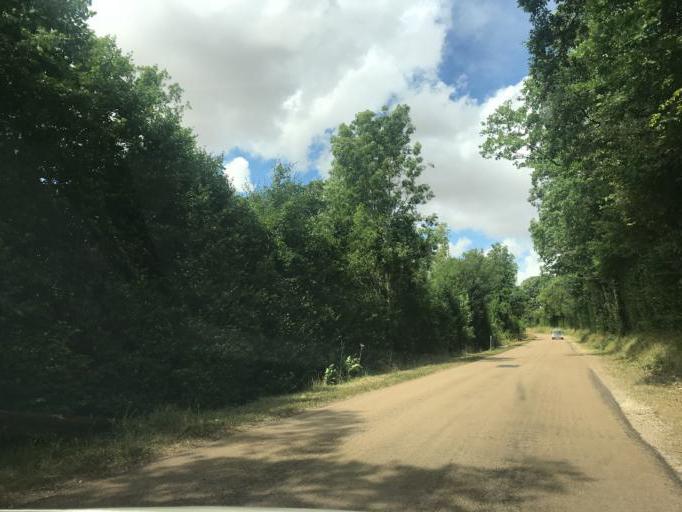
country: FR
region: Bourgogne
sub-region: Departement de l'Yonne
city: Fontenailles
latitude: 47.5618
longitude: 3.3389
